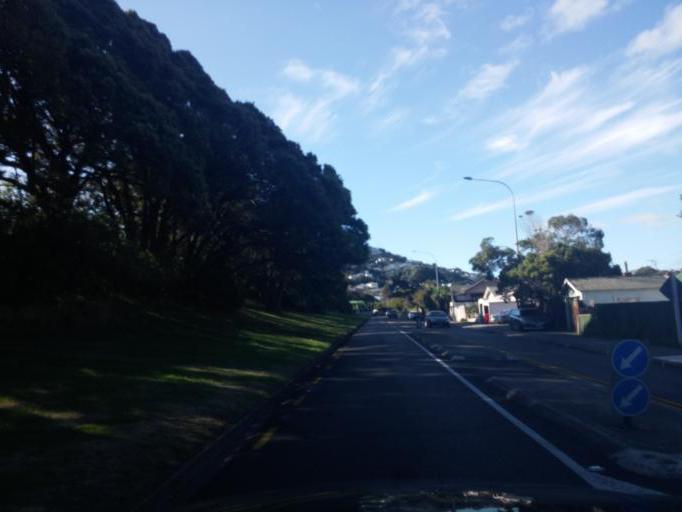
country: NZ
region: Wellington
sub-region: Wellington City
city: Wellington
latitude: -41.3083
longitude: 174.7917
